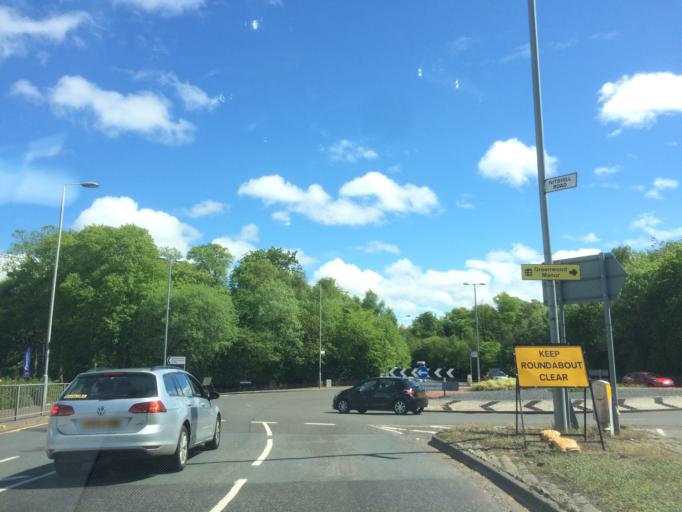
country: GB
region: Scotland
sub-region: East Renfrewshire
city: Giffnock
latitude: 55.8007
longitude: -4.3234
